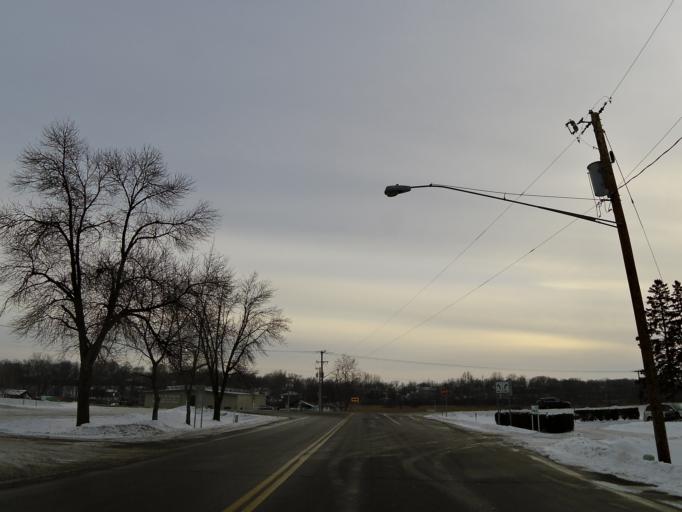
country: US
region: Minnesota
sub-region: Carver County
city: Victoria
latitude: 44.8622
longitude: -93.6719
